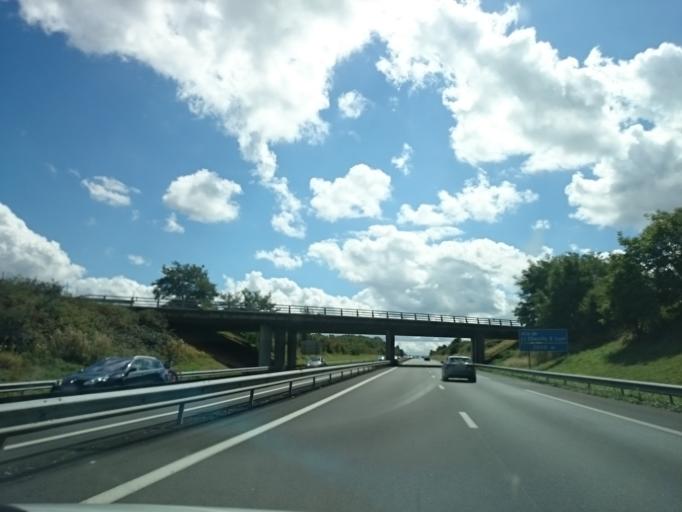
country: FR
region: Pays de la Loire
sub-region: Departement de Maine-et-Loire
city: Durtal
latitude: 47.6454
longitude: -0.2741
